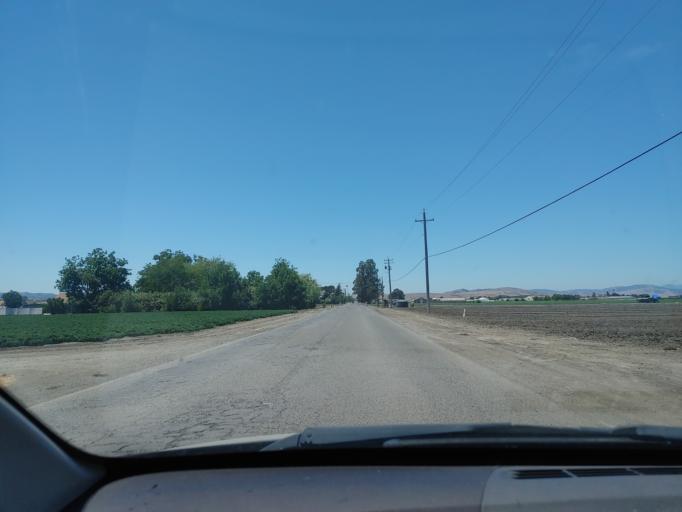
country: US
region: California
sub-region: San Benito County
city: Hollister
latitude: 36.8688
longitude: -121.3878
